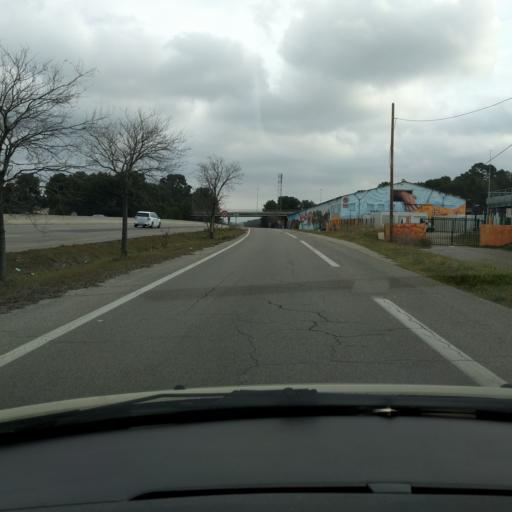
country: FR
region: Provence-Alpes-Cote d'Azur
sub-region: Departement des Bouches-du-Rhone
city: Simiane-Collongue
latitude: 43.4345
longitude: 5.4245
